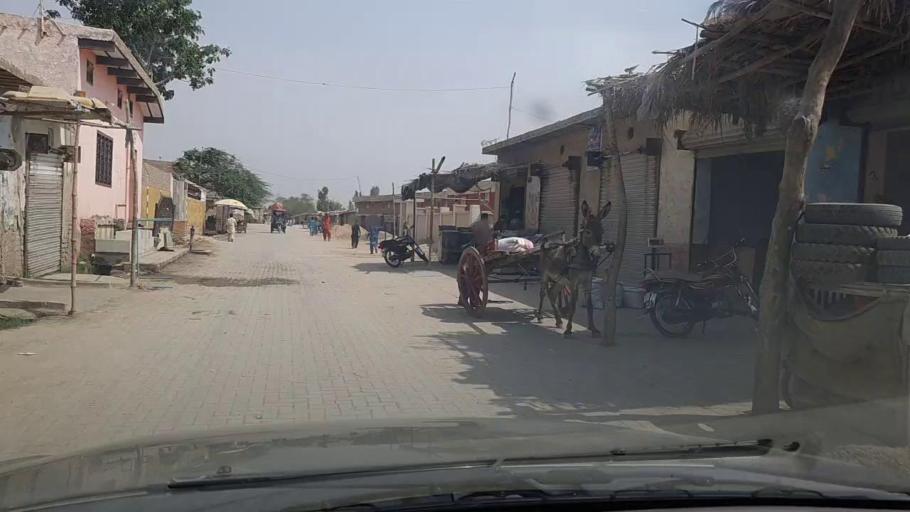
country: PK
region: Sindh
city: Shikarpur
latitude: 27.9290
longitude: 68.6622
